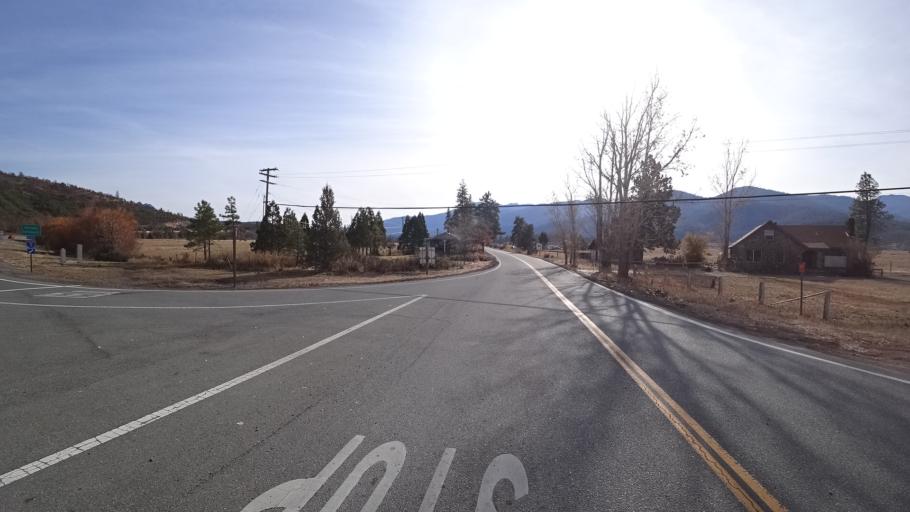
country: US
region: California
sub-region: Siskiyou County
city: Weed
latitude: 41.4404
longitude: -122.4352
